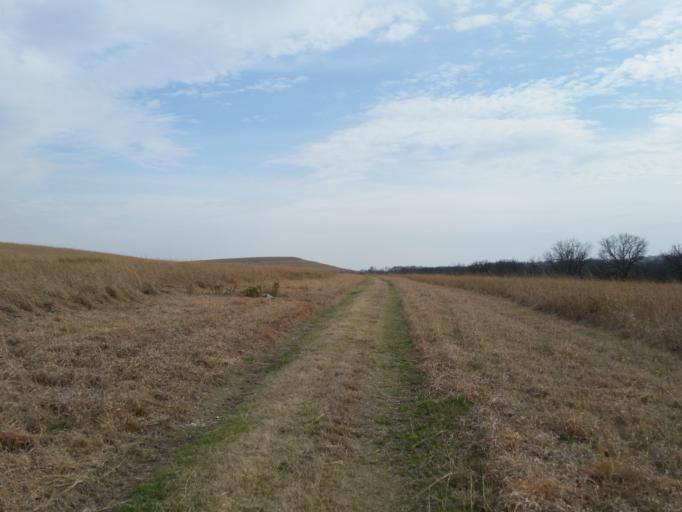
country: US
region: Kansas
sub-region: Chase County
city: Cottonwood Falls
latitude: 38.4357
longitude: -96.5472
